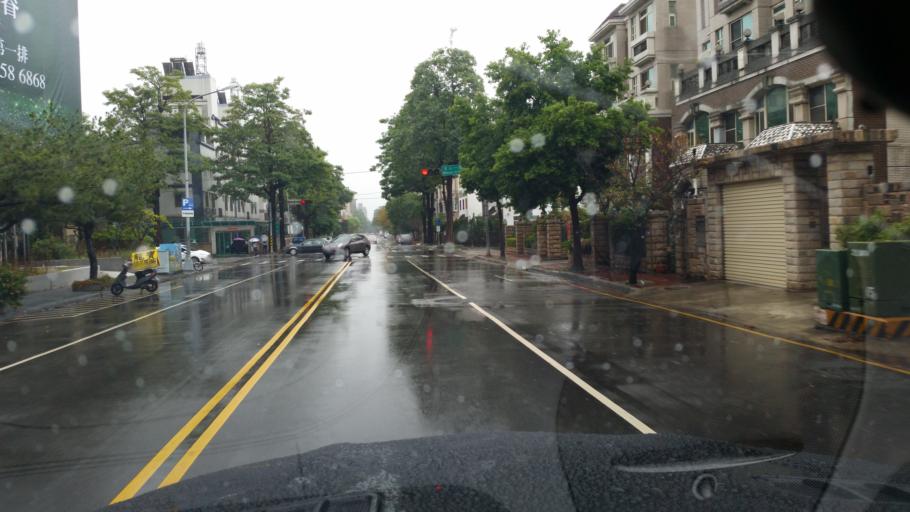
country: TW
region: Taiwan
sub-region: Taichung City
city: Taichung
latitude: 24.1552
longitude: 120.6439
